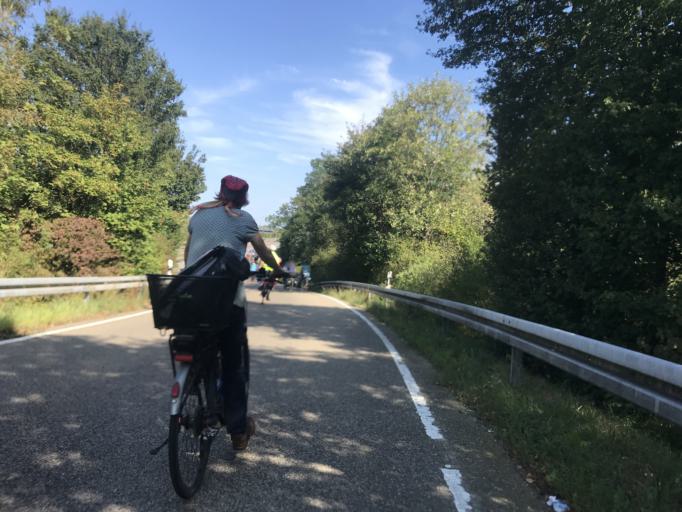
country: DE
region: Hesse
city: Kelsterbach
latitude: 50.0761
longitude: 8.5466
